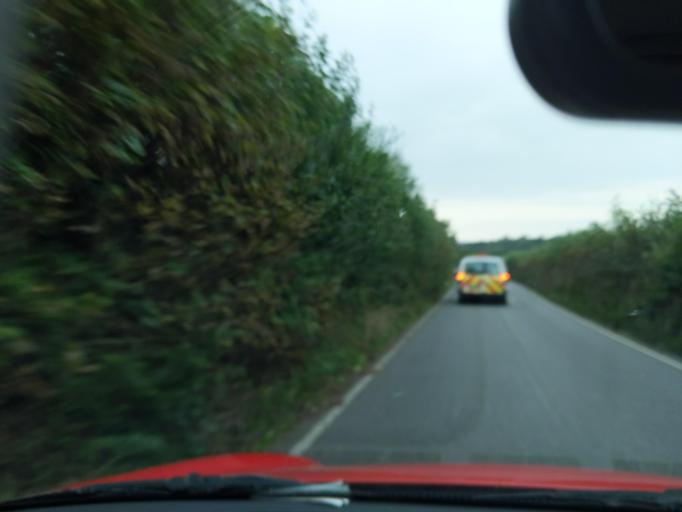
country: GB
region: England
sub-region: Devon
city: Great Torrington
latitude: 50.8692
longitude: -4.0727
